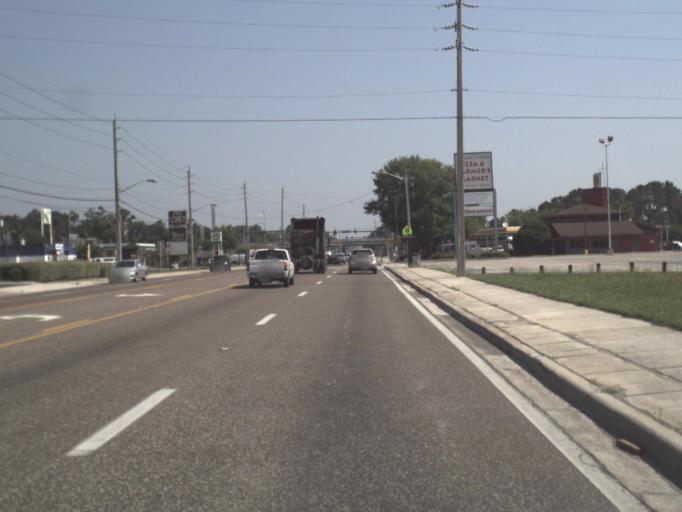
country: US
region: Florida
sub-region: Duval County
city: Jacksonville
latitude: 30.3124
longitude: -81.7519
